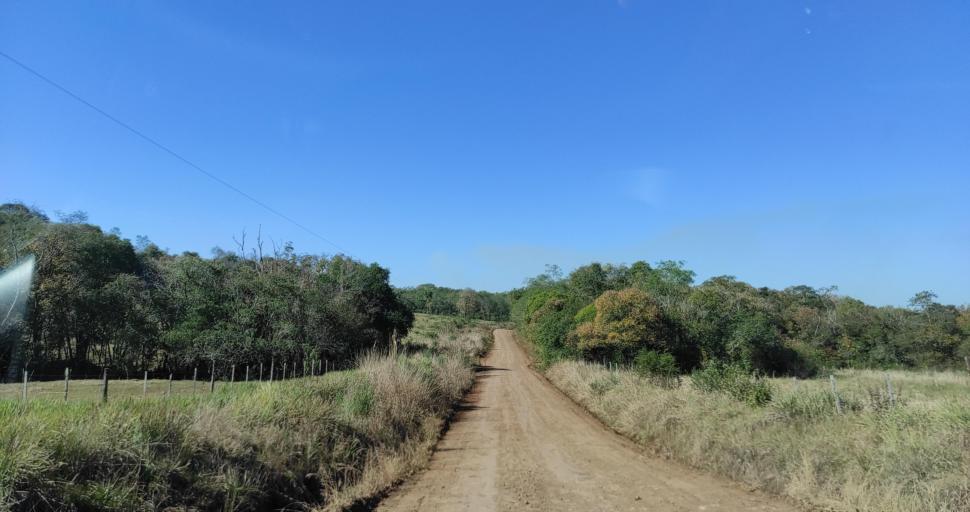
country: AR
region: Misiones
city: Cerro Cora
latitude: -27.6303
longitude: -55.7008
